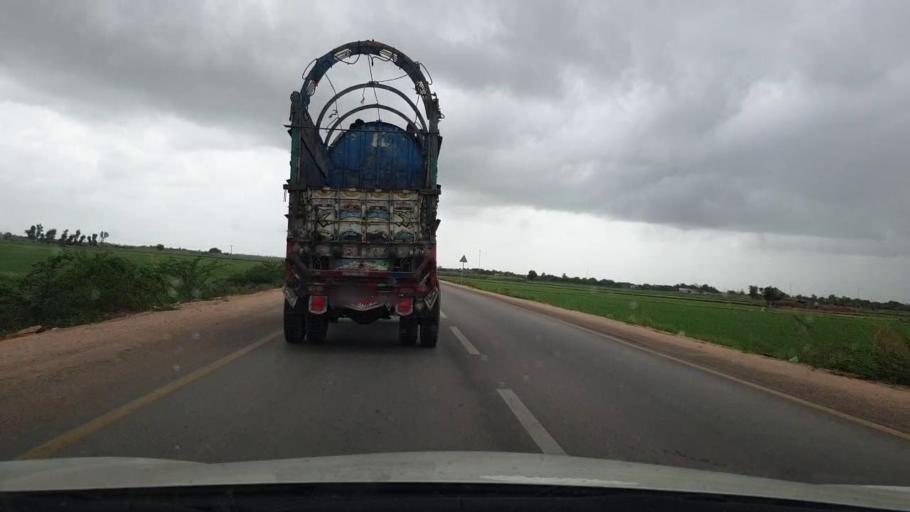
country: PK
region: Sindh
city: Kario
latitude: 24.6465
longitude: 68.4908
